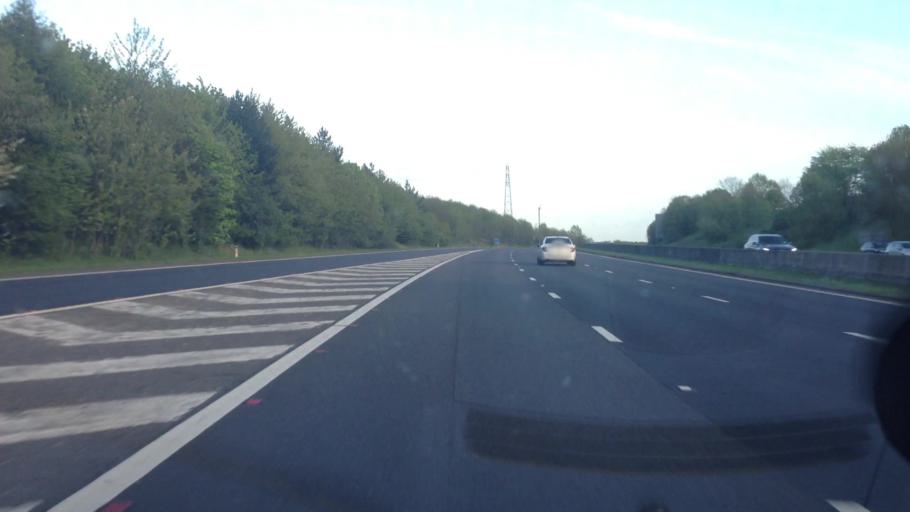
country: GB
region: England
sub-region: Barnsley
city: Birdwell
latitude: 53.4945
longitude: -1.4729
